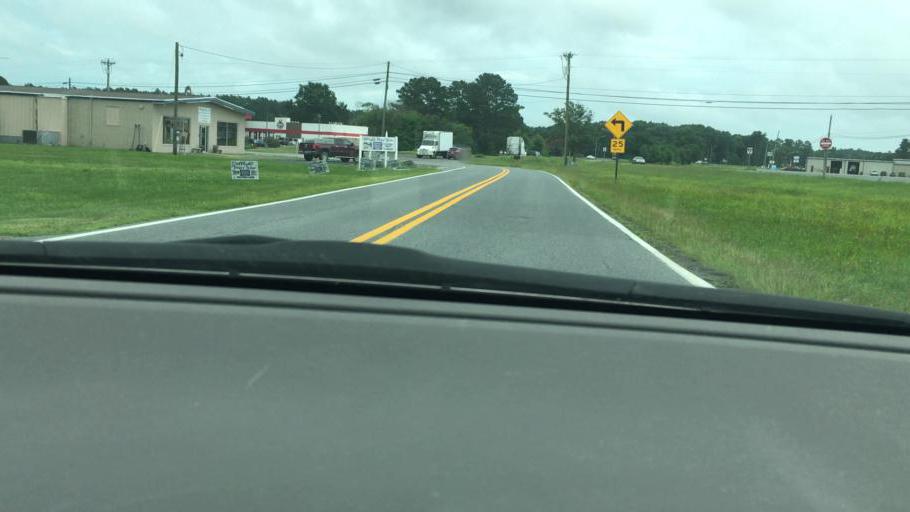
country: US
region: Maryland
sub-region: Worcester County
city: Pocomoke City
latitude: 38.0616
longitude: -75.5484
